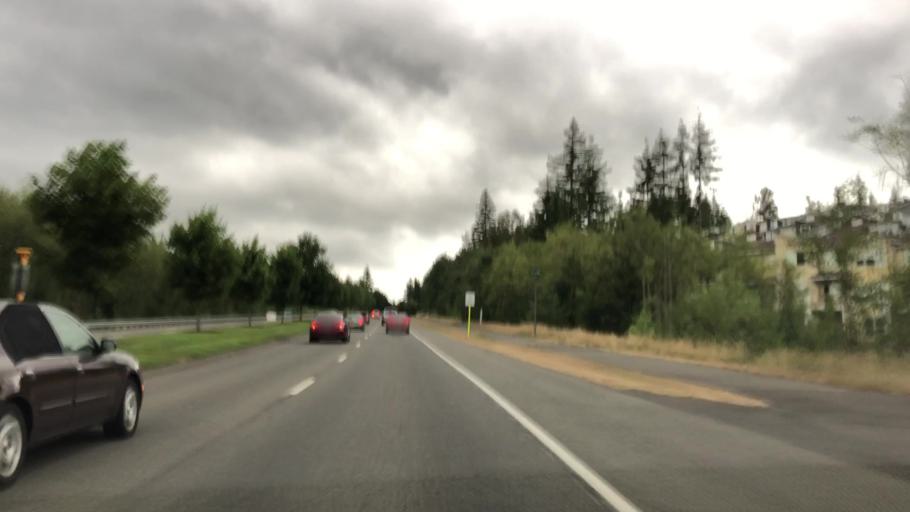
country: US
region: Washington
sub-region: King County
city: Fall City
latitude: 47.5223
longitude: -121.8801
